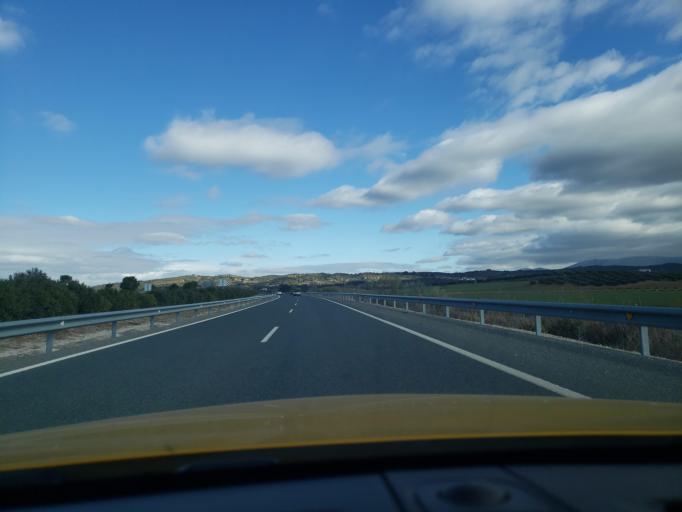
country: ES
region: Andalusia
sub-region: Provincia de Malaga
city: Villanueva del Trabuco
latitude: 37.0719
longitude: -4.3231
